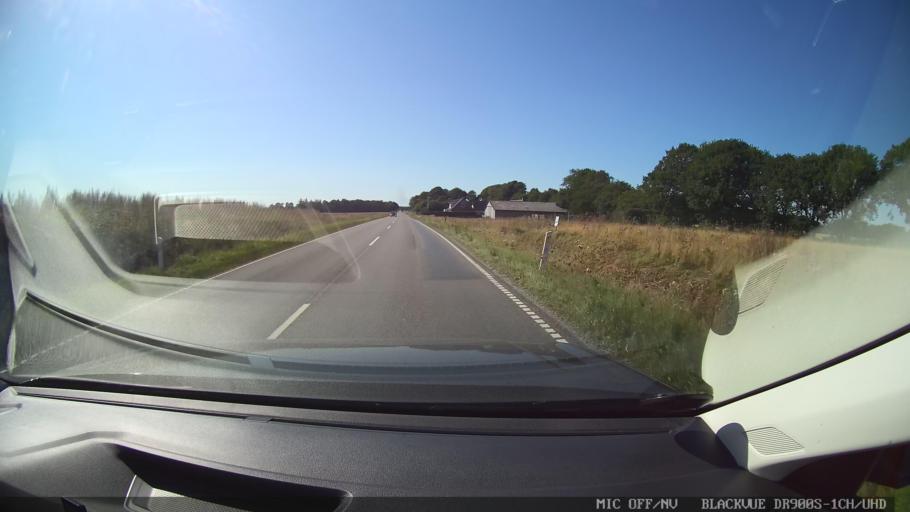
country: DK
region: North Denmark
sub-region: Mariagerfjord Kommune
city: Mariager
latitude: 56.6345
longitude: 9.9149
